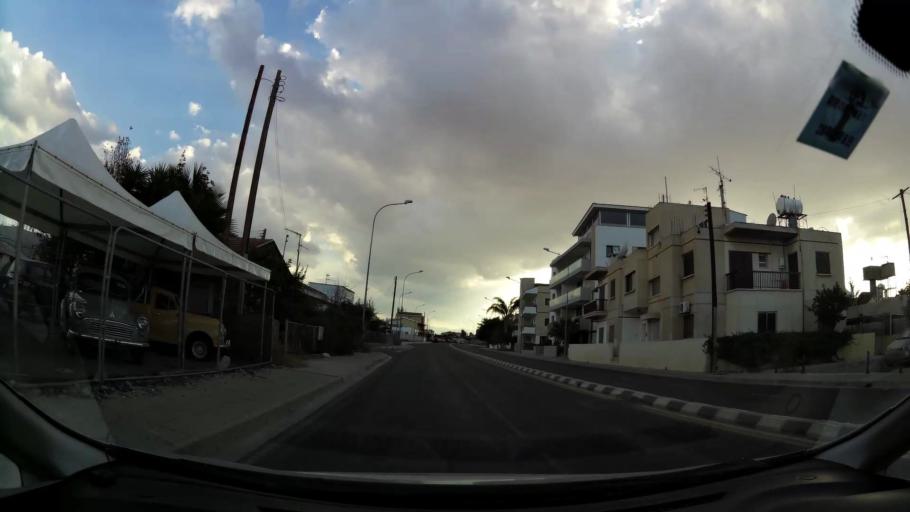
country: CY
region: Lefkosia
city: Tseri
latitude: 35.1173
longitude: 33.3139
